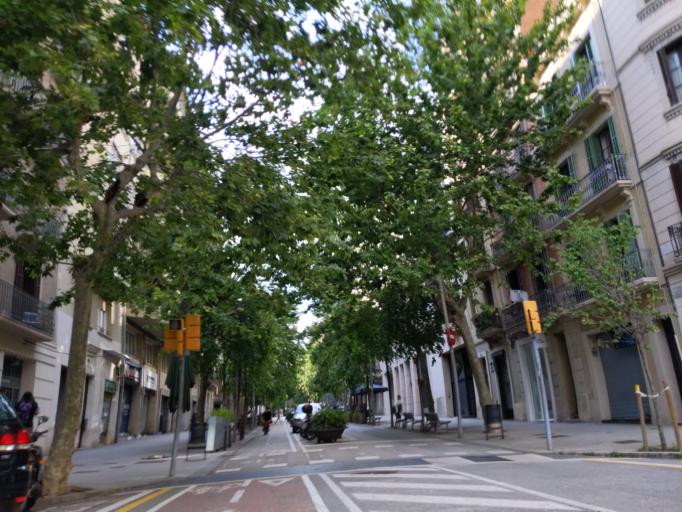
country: ES
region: Catalonia
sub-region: Provincia de Barcelona
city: Barcelona
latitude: 41.3925
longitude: 2.1562
